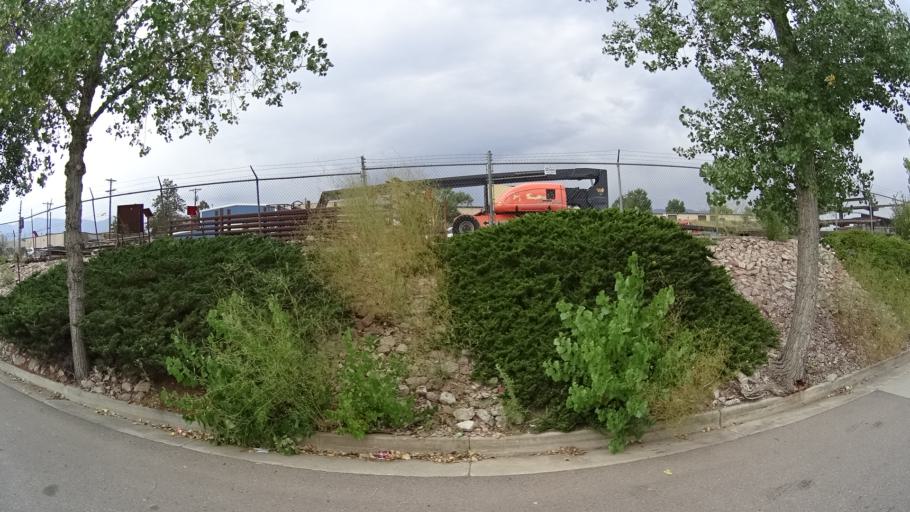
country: US
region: Colorado
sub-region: El Paso County
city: Colorado Springs
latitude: 38.8902
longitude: -104.8302
